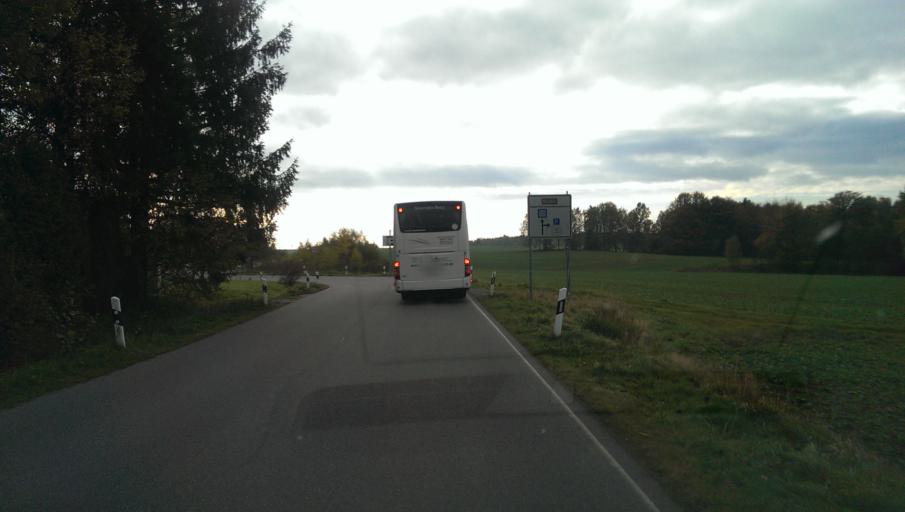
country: DE
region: Saxony
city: Stadt Wehlen
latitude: 50.9868
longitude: 14.0529
